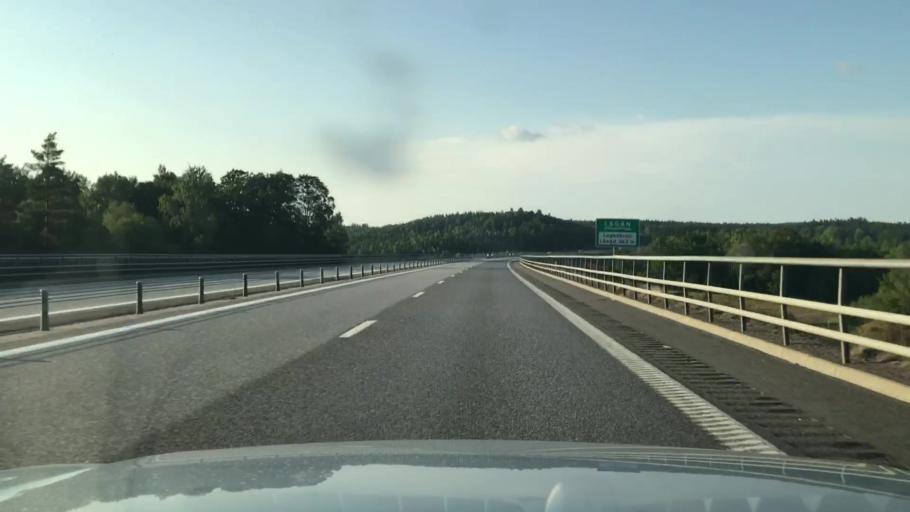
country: SE
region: Kronoberg
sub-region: Markaryds Kommun
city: Markaryd
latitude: 56.4993
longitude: 13.6530
